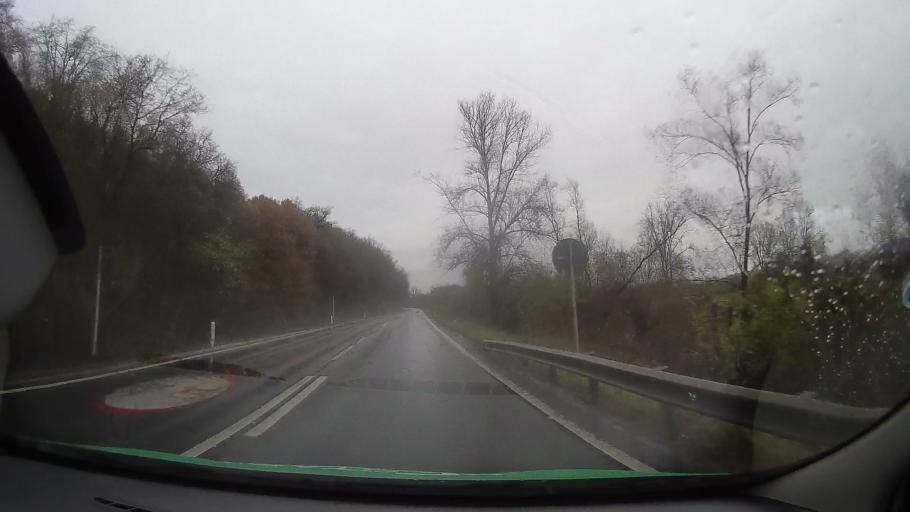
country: RO
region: Mures
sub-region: Comuna Brancovenesti
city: Brancovenesti
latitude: 46.8679
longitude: 24.7695
